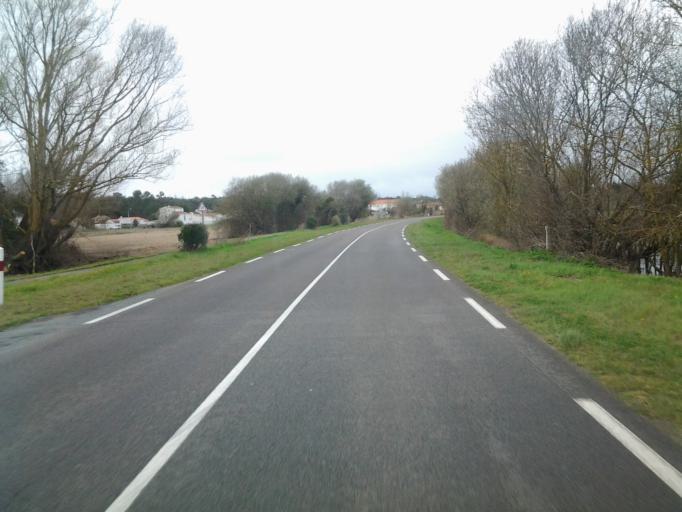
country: FR
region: Pays de la Loire
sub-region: Departement de la Vendee
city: La Tranche-sur-Mer
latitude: 46.3641
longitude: -1.4548
